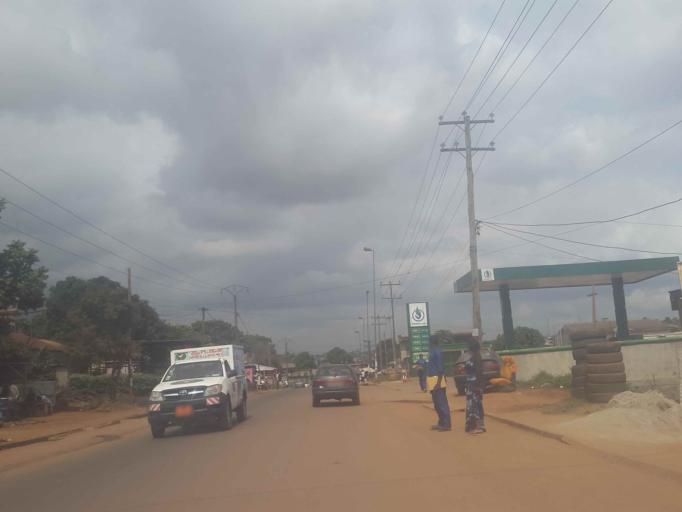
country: CM
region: Centre
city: Yaounde
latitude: 3.8740
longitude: 11.4772
